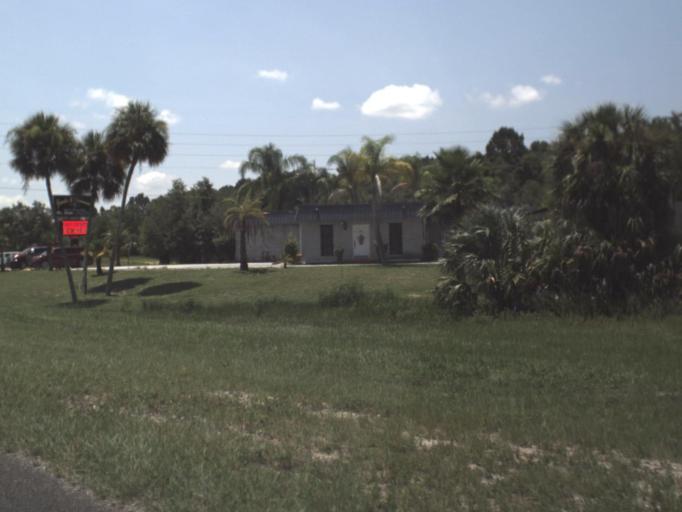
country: US
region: Florida
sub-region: Citrus County
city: Homosassa Springs
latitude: 28.7932
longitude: -82.5713
